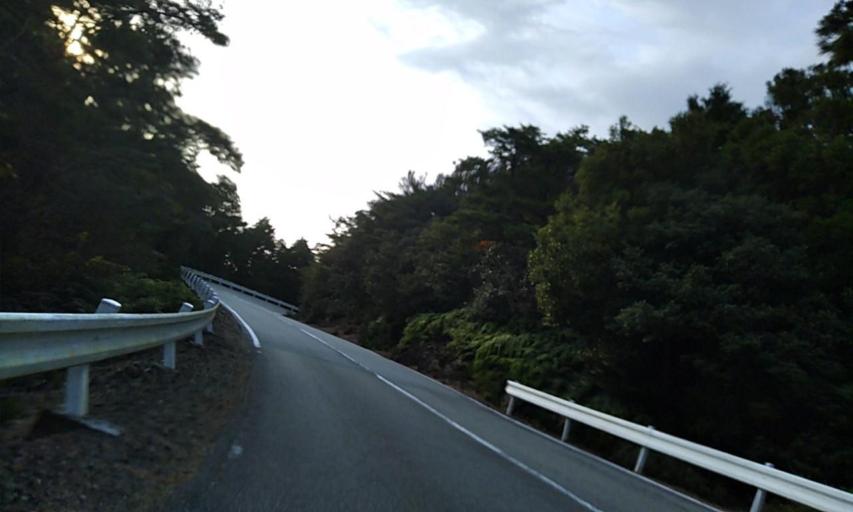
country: JP
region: Mie
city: Toba
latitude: 34.4595
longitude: 136.7765
